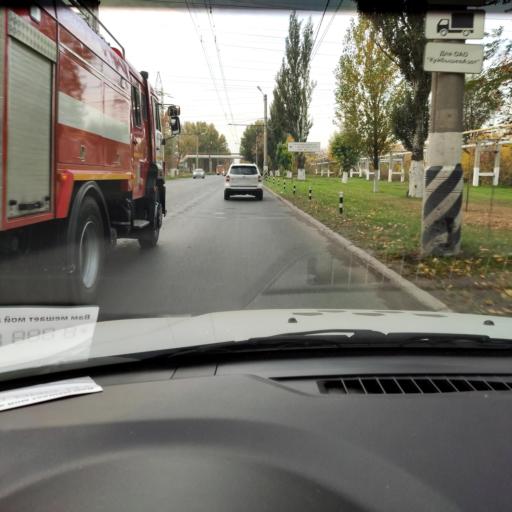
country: RU
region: Samara
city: Tol'yatti
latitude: 53.5527
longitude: 49.4494
